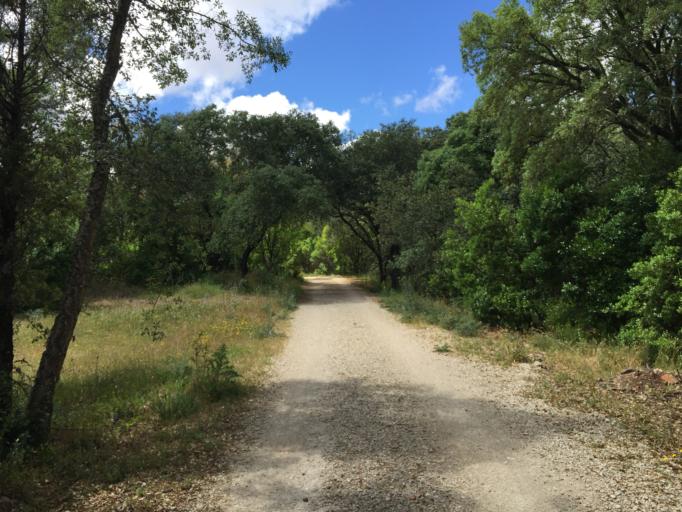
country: PT
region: Lisbon
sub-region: Odivelas
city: Pontinha
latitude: 38.7368
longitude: -9.1900
